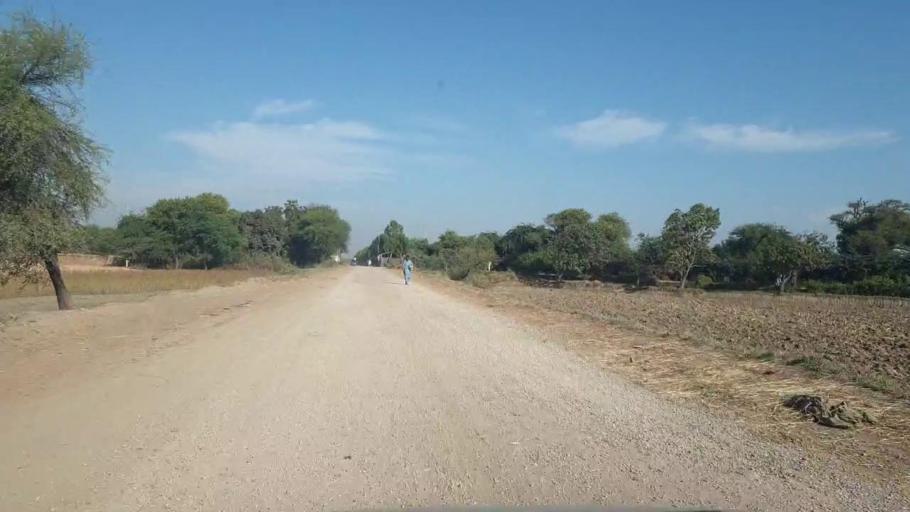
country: PK
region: Sindh
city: Talhar
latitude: 24.9441
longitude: 68.7874
